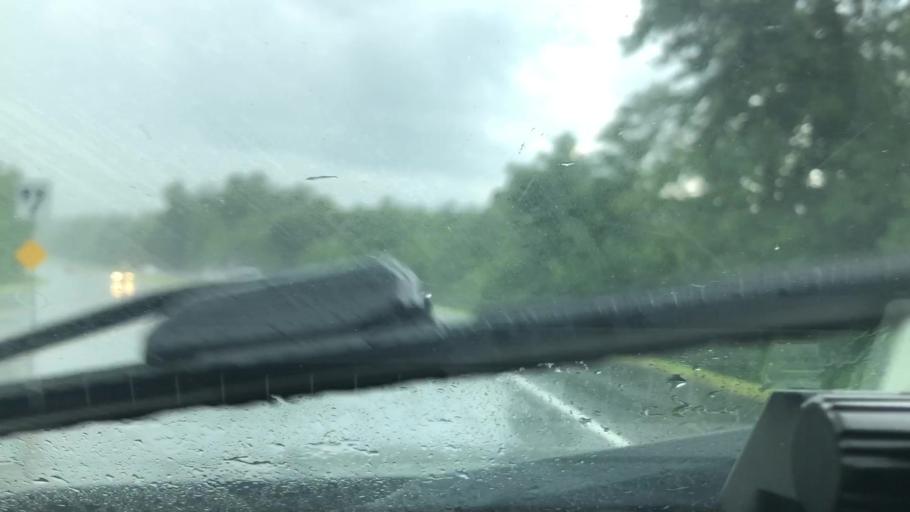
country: US
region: Pennsylvania
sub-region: Lehigh County
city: Fountain Hill
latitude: 40.5675
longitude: -75.3972
